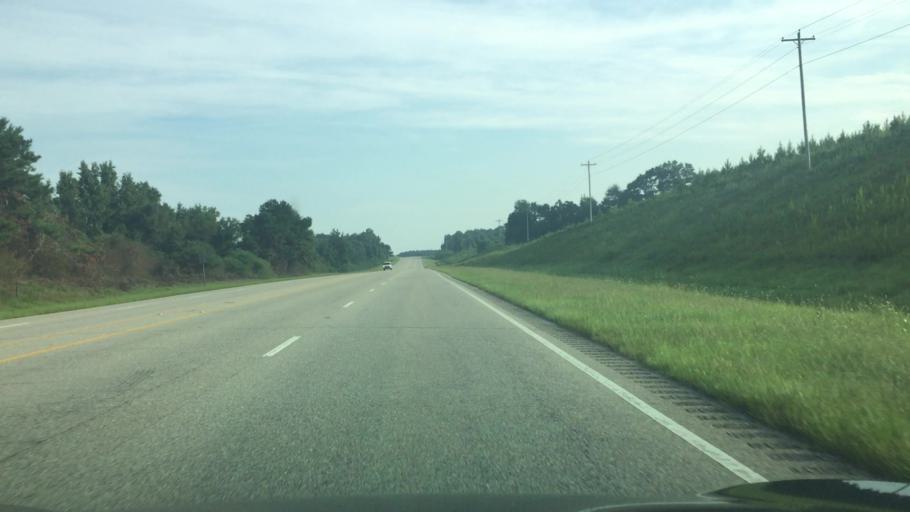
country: US
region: Alabama
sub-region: Covington County
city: Andalusia
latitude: 31.4270
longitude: -86.6116
